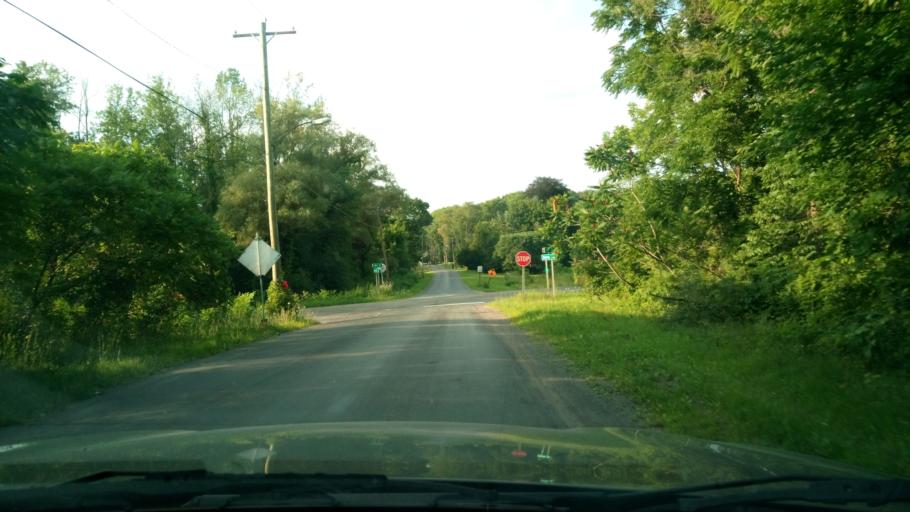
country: US
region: New York
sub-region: Wayne County
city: Lyons
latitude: 43.0769
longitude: -76.9468
